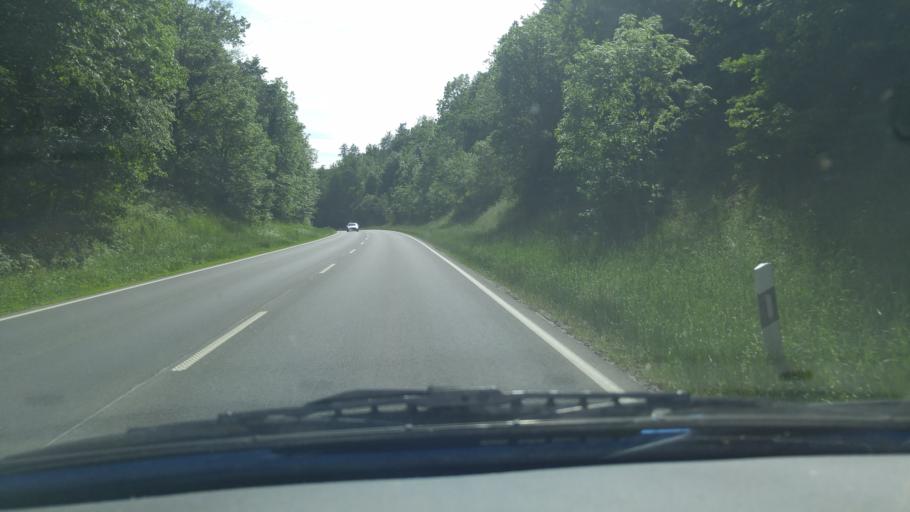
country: DE
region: Hesse
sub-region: Regierungsbezirk Giessen
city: Schotten
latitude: 50.4853
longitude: 9.0983
